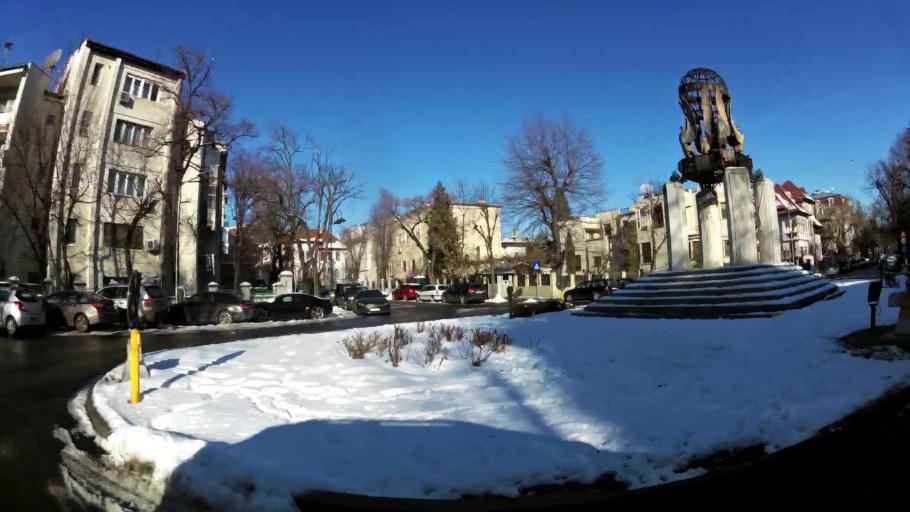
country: RO
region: Bucuresti
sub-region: Municipiul Bucuresti
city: Bucharest
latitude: 44.4570
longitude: 26.0913
